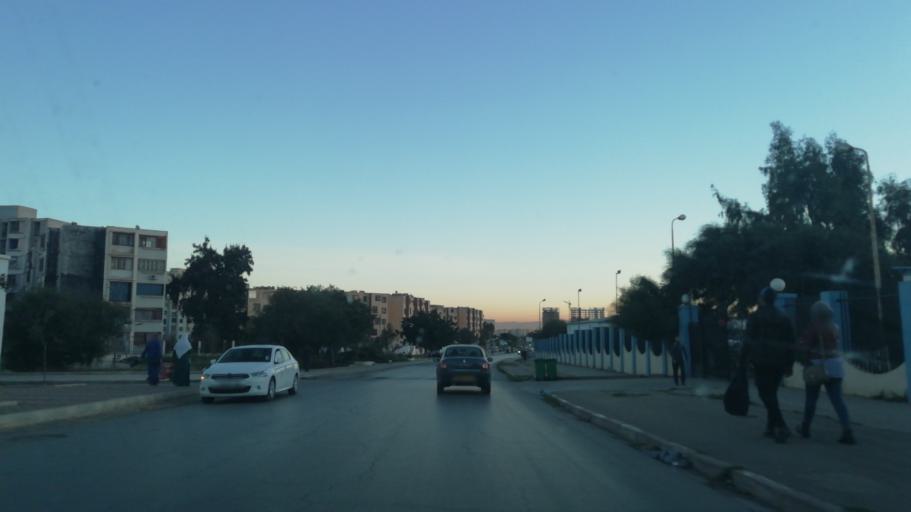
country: DZ
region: Oran
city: Bir el Djir
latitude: 35.7070
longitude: -0.5911
